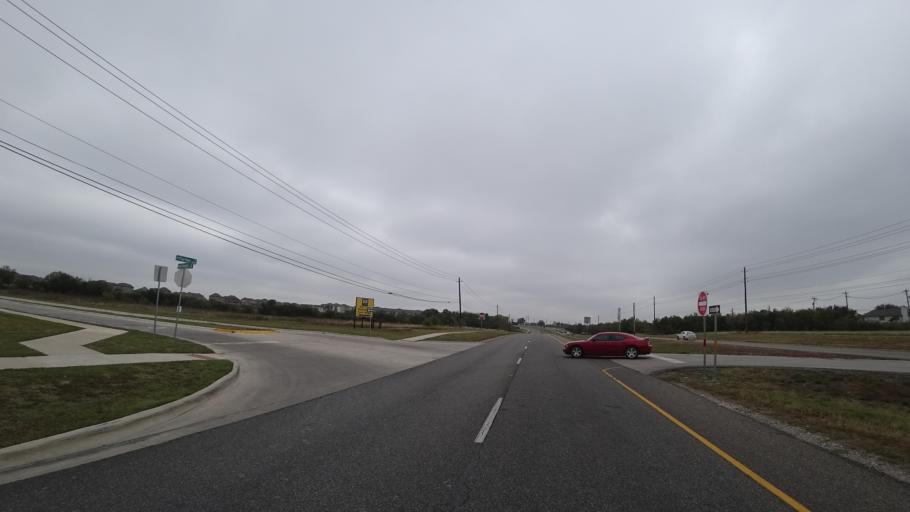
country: US
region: Texas
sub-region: Travis County
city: Pflugerville
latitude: 30.3947
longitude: -97.6535
